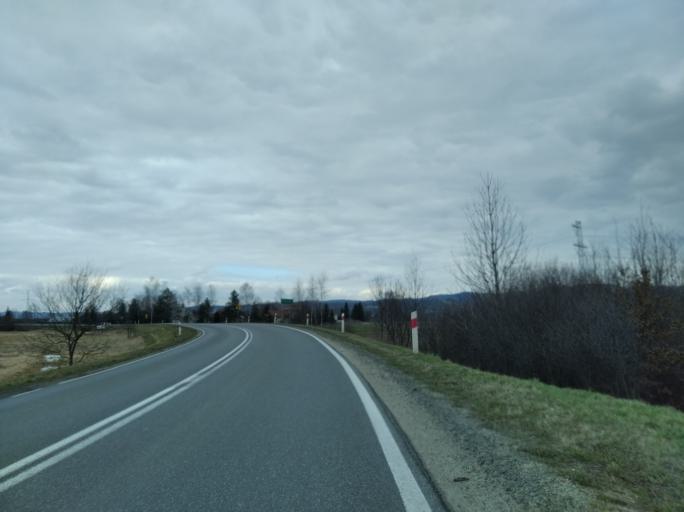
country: PL
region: Subcarpathian Voivodeship
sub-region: Powiat krosnienski
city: Wojaszowka
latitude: 49.7900
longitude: 21.6597
